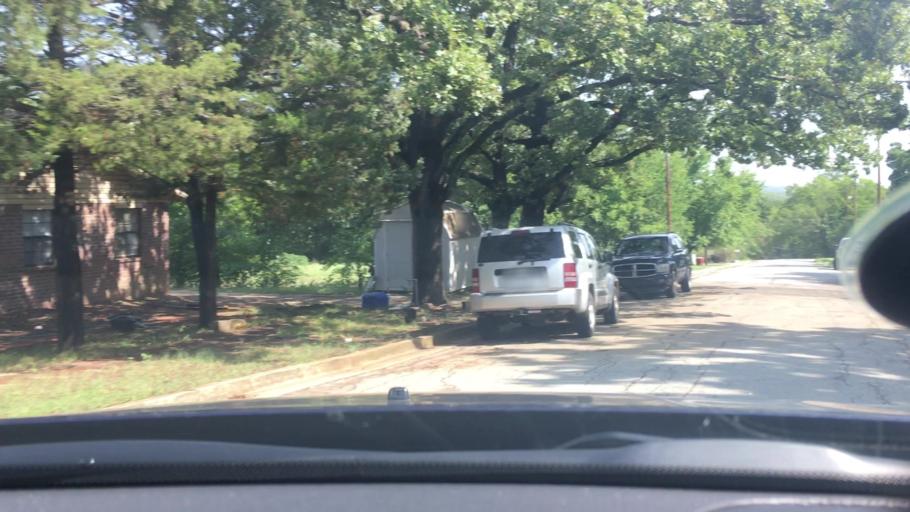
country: US
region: Oklahoma
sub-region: Atoka County
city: Atoka
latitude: 34.3872
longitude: -96.1315
